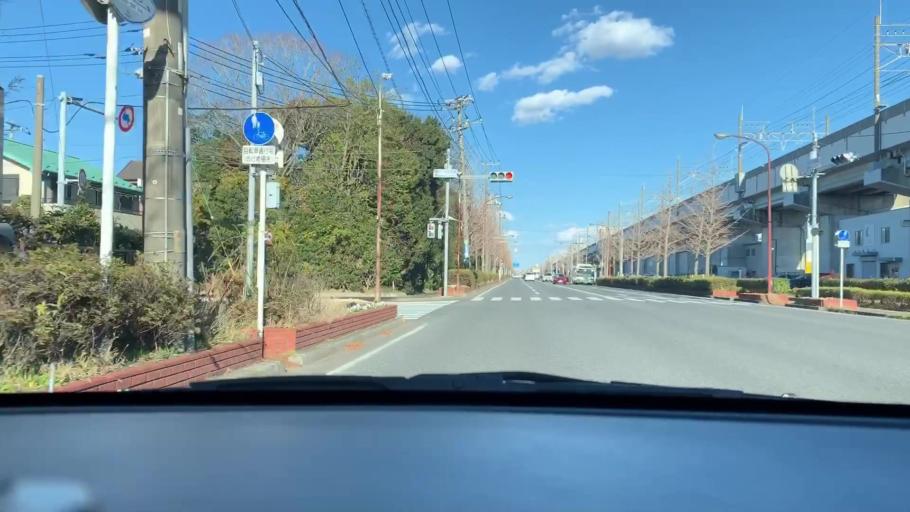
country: JP
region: Tokyo
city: Urayasu
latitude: 35.6377
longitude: 139.8977
